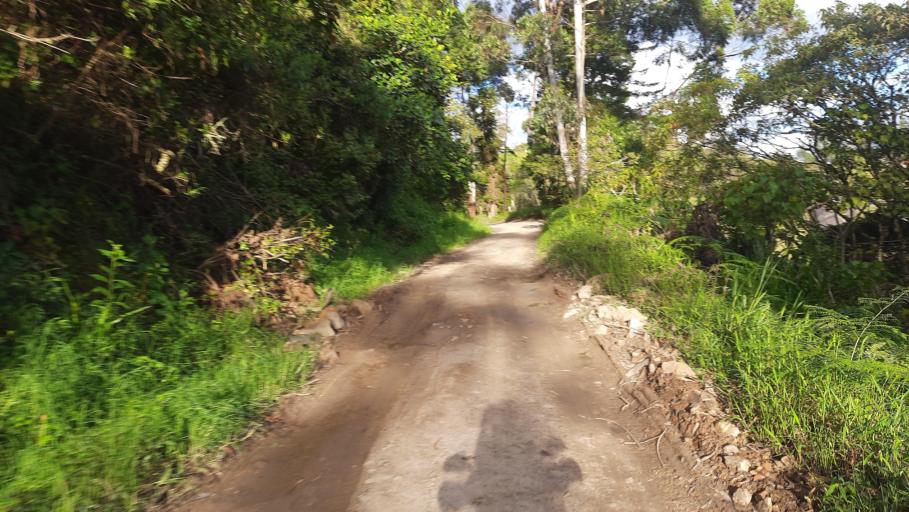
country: CO
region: Cundinamarca
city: Tenza
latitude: 5.1029
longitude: -73.4206
